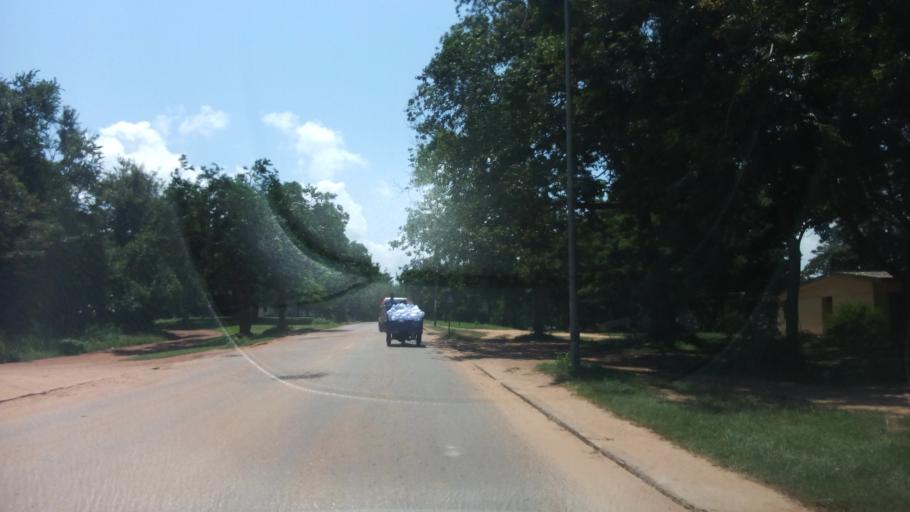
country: GH
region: Central
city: Cape Coast
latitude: 5.1224
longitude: -1.2915
